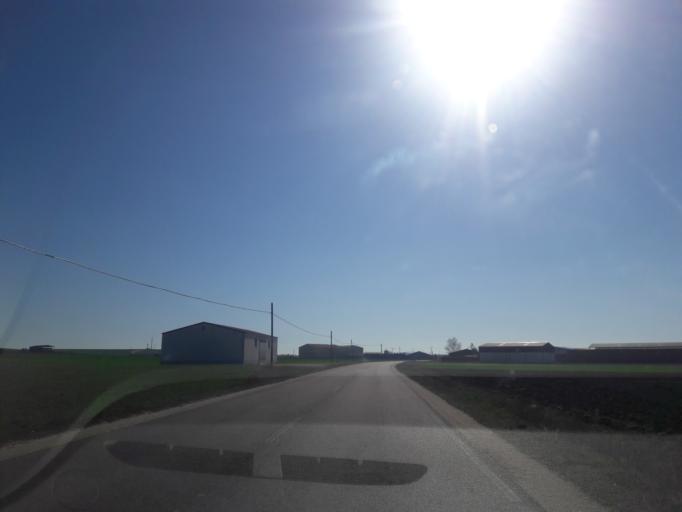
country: ES
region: Castille and Leon
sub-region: Provincia de Salamanca
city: Macotera
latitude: 40.8345
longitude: -5.2989
